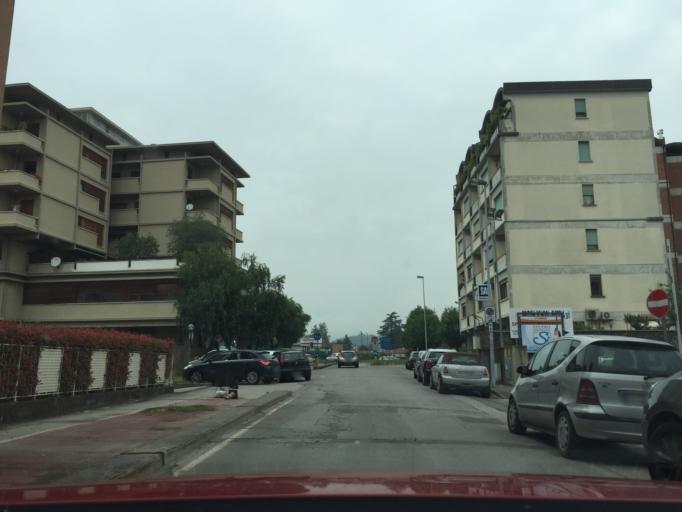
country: IT
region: Tuscany
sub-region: Provincia di Pistoia
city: Pistoia
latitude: 43.9394
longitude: 10.9136
